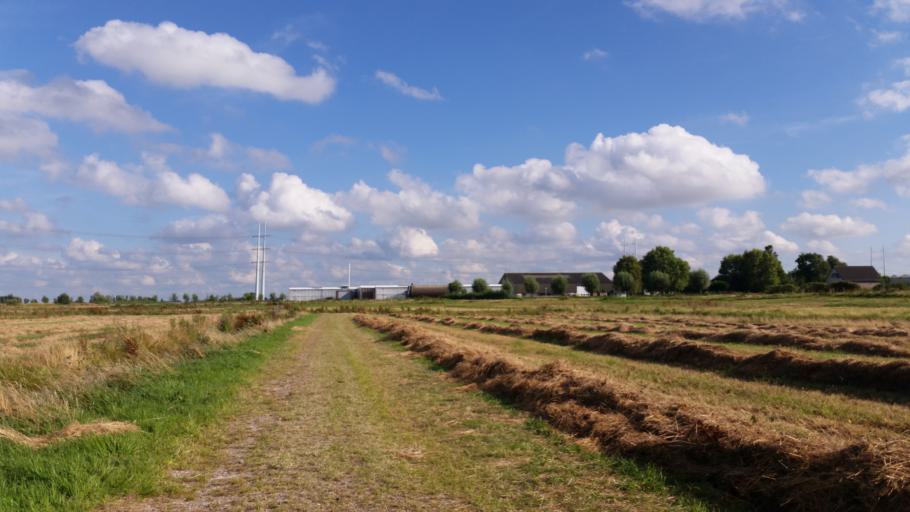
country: NL
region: South Holland
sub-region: Gemeente Zoetermeer
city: Zoetermeer
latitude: 52.0308
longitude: 4.4664
